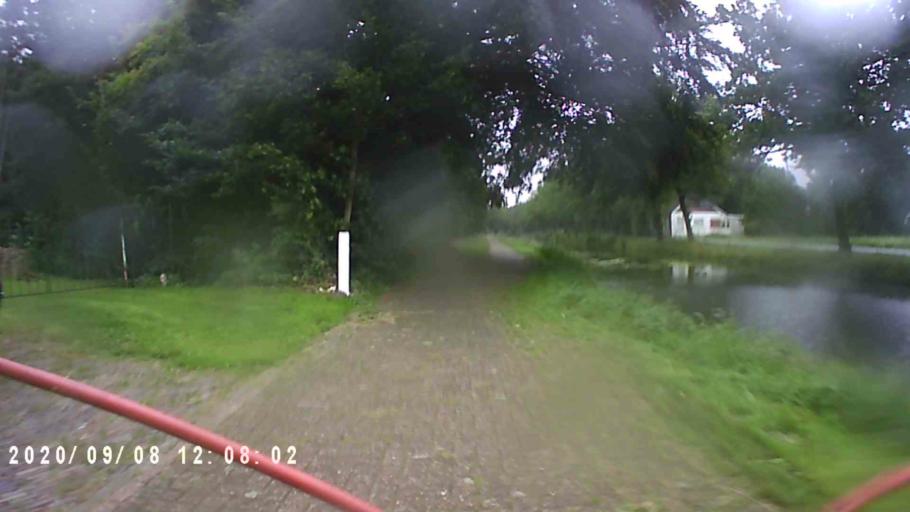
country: NL
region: Groningen
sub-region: Gemeente Veendam
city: Veendam
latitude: 53.1039
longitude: 6.8290
